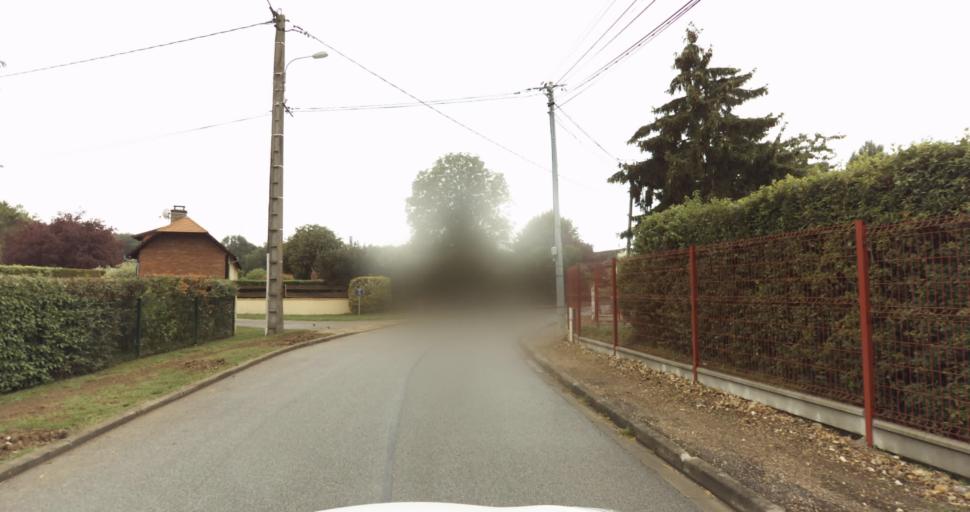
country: FR
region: Haute-Normandie
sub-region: Departement de l'Eure
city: Normanville
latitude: 49.0972
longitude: 1.1503
